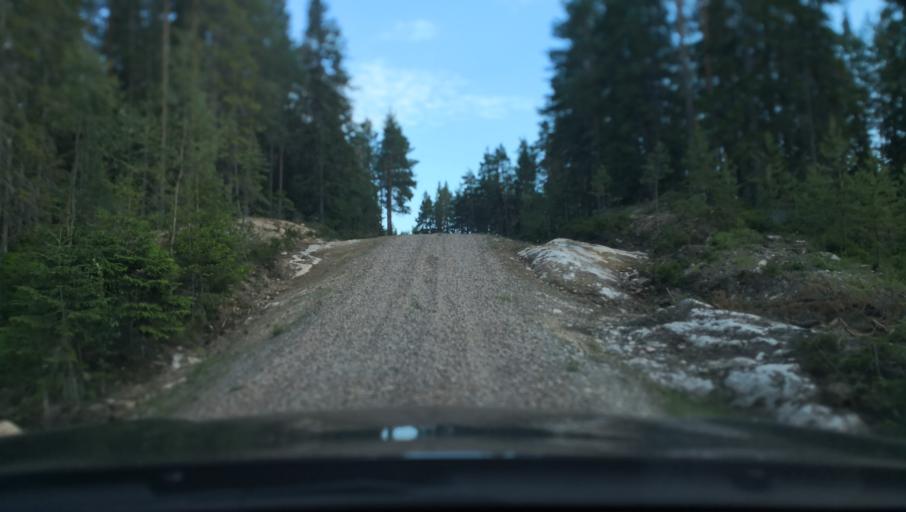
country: SE
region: Dalarna
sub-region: Smedjebackens Kommun
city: Smedjebacken
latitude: 60.0678
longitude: 15.3074
